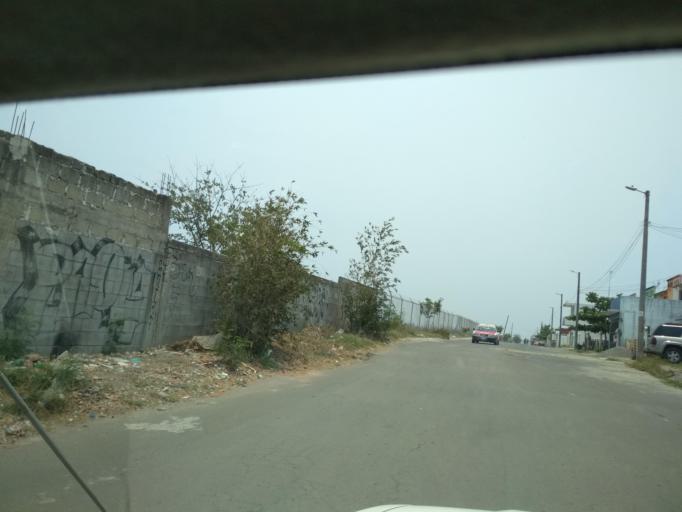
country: MX
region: Veracruz
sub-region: Veracruz
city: Las Amapolas
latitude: 19.1556
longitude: -96.2132
